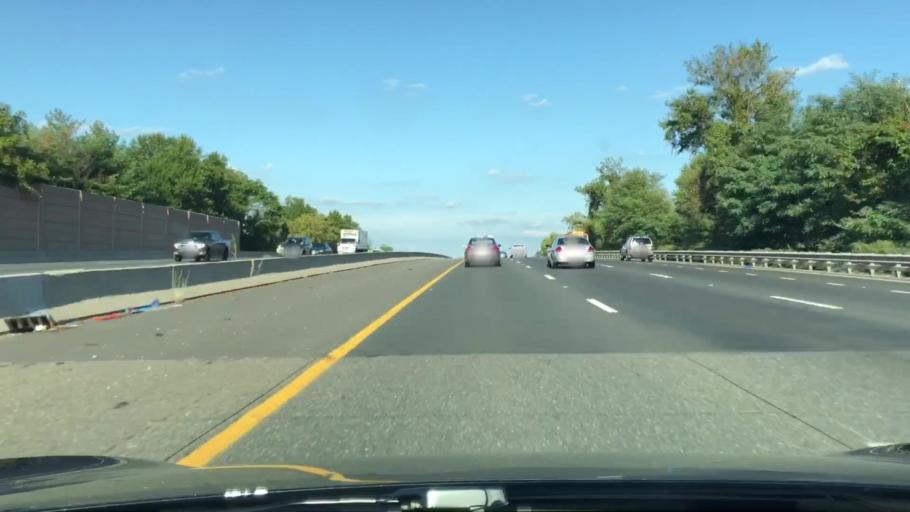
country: US
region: New Jersey
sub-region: Gloucester County
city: National Park
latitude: 39.8411
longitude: -75.1916
